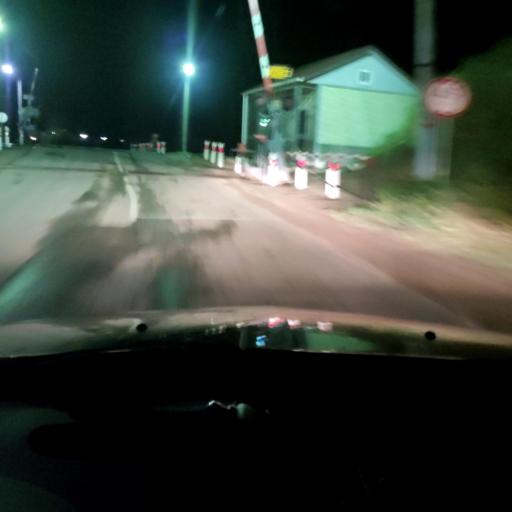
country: RU
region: Voronezj
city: Khrenovoye
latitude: 51.1182
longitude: 40.2631
